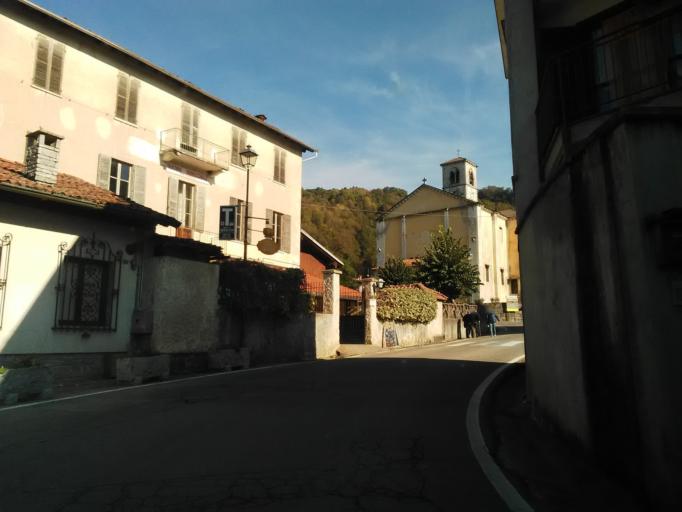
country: IT
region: Piedmont
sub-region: Provincia di Vercelli
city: Postua
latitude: 45.7128
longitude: 8.2301
